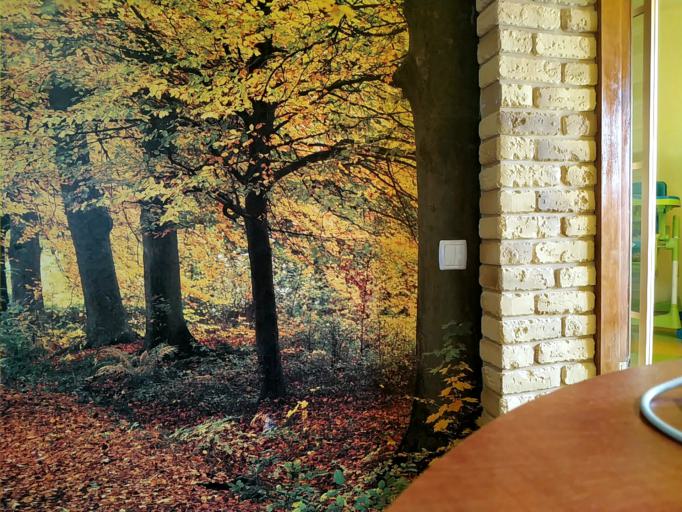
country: RU
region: Tverskaya
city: Kalashnikovo
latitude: 57.3339
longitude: 35.3345
